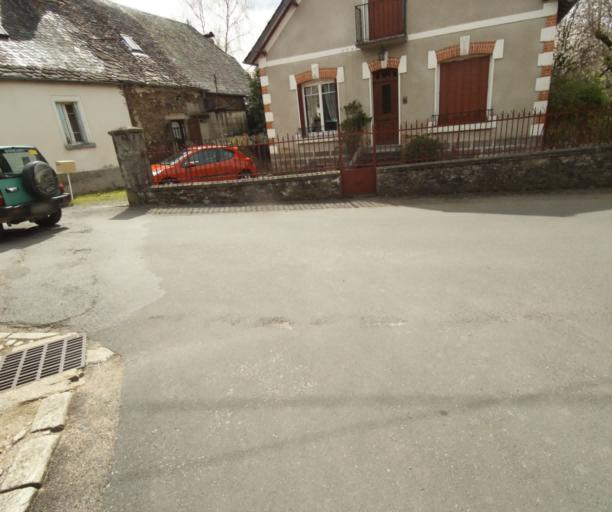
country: FR
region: Limousin
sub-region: Departement de la Correze
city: Laguenne
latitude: 45.2197
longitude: 1.8668
